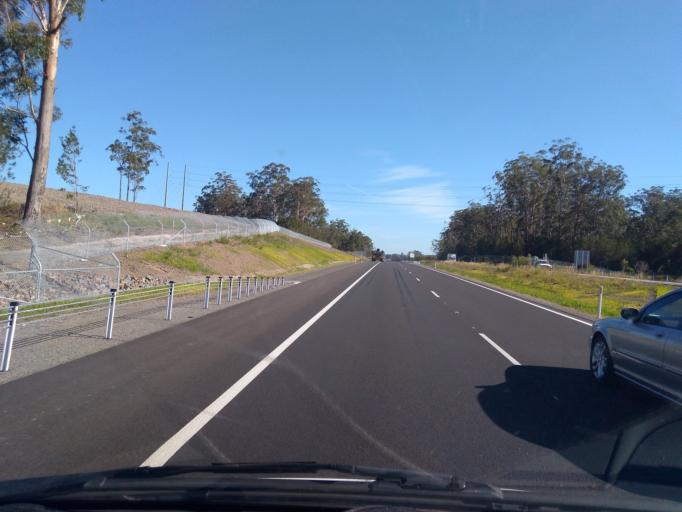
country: AU
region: New South Wales
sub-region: Kempsey
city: Kempsey
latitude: -31.2305
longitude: 152.8235
